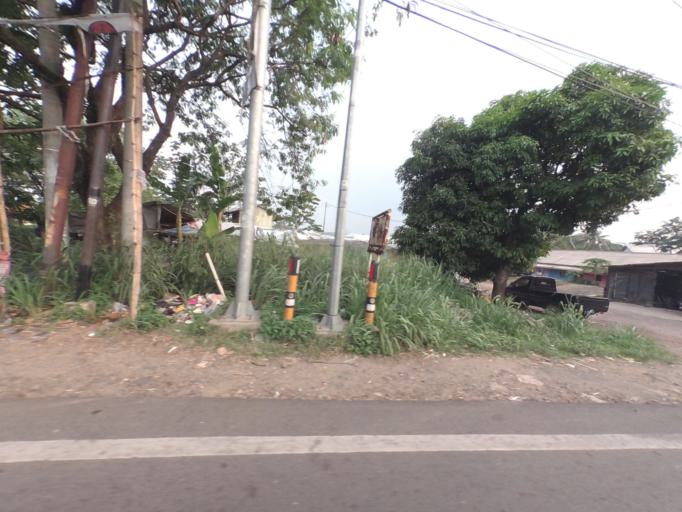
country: ID
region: West Java
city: Ciampea
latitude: -6.5691
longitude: 106.6690
